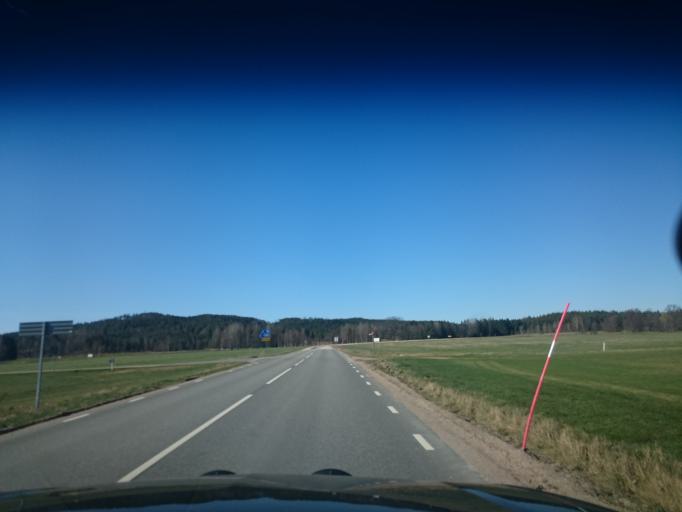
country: SE
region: Joenkoeping
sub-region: Vetlanda Kommun
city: Landsbro
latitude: 57.2060
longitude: 14.9465
